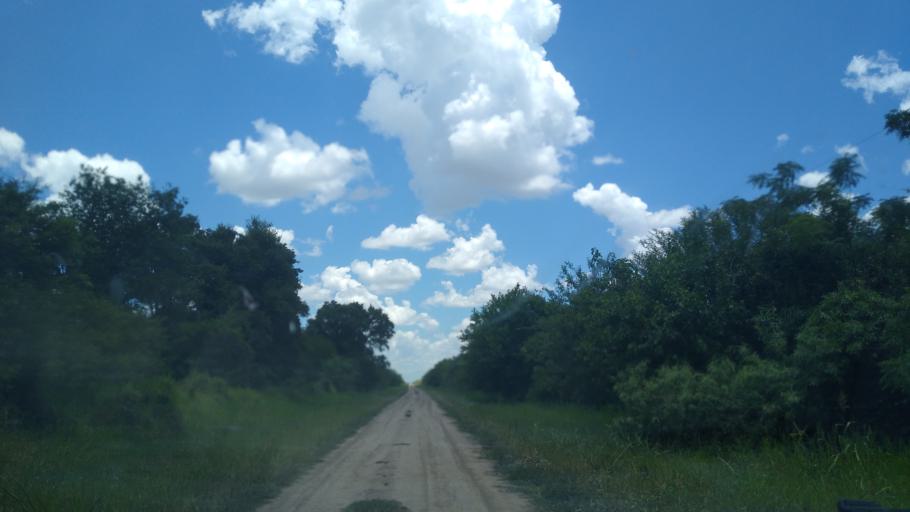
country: AR
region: Chaco
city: Presidencia Roque Saenz Pena
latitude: -26.7479
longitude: -60.3377
